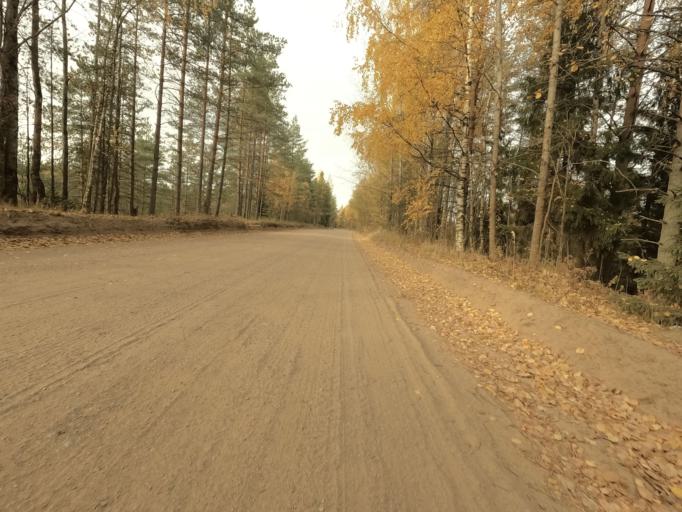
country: RU
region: Leningrad
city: Priladozhskiy
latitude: 59.6787
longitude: 31.3647
